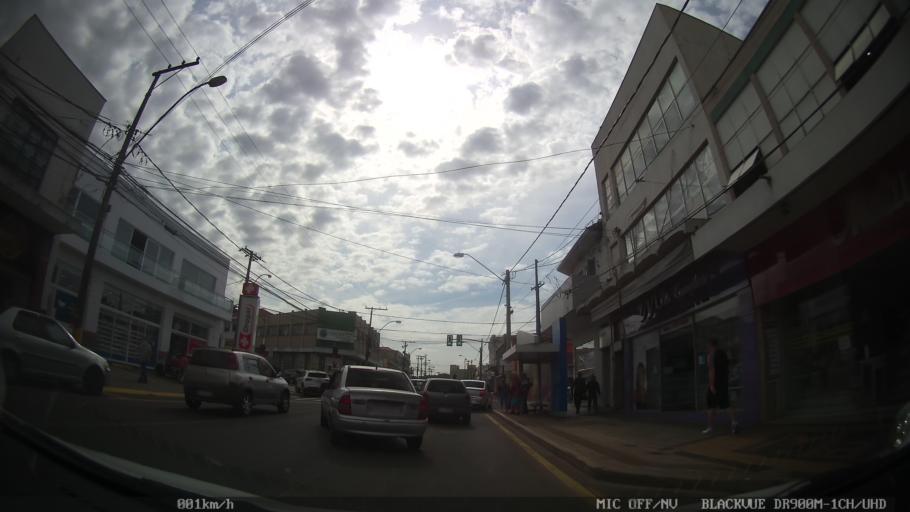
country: BR
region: Sao Paulo
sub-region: Piracicaba
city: Piracicaba
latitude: -22.7089
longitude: -47.6537
